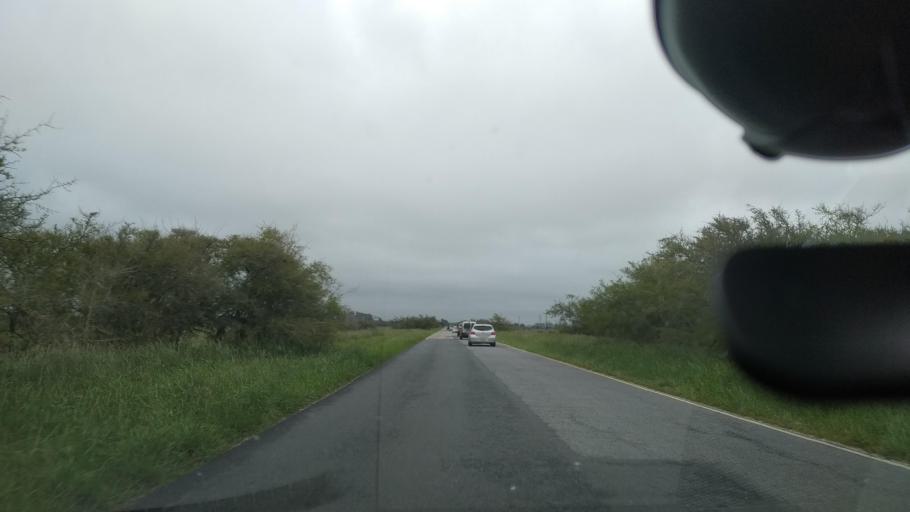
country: AR
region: Buenos Aires
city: Veronica
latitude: -35.5465
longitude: -57.3124
